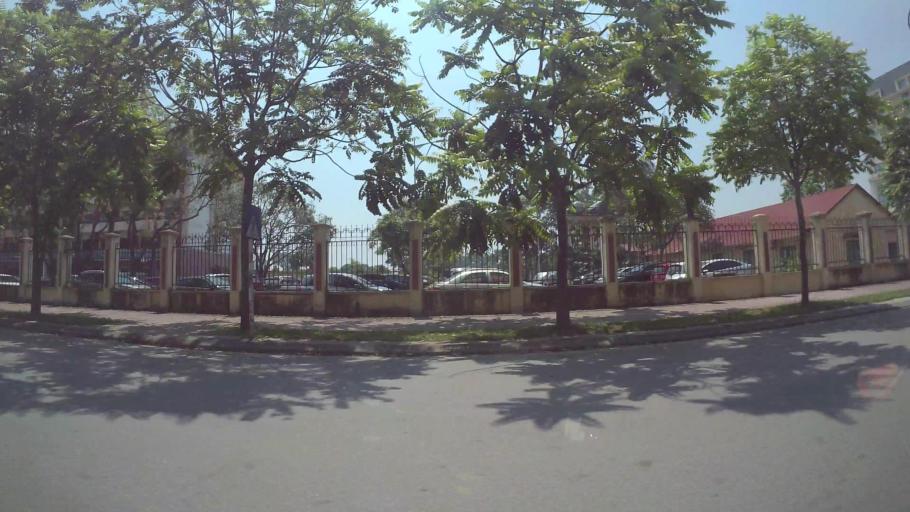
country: VN
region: Ha Noi
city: Hoan Kiem
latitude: 21.0428
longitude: 105.8818
